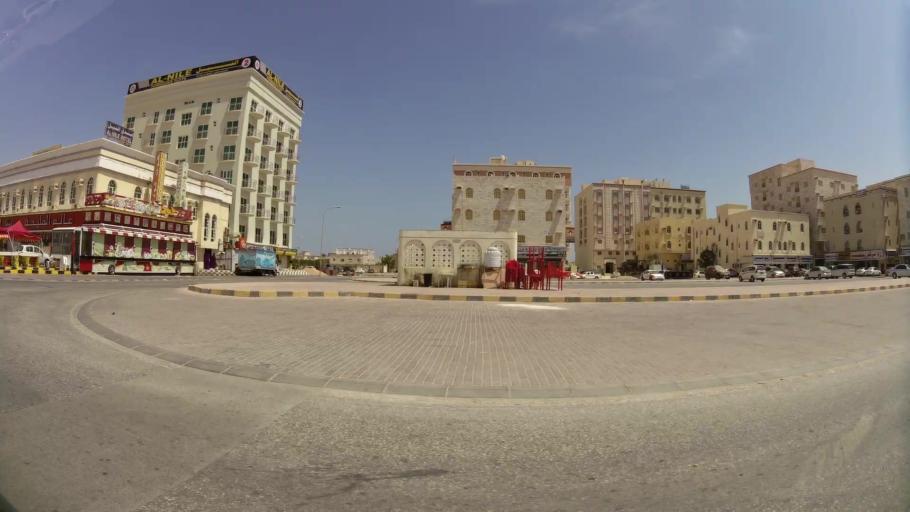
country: OM
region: Zufar
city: Salalah
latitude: 17.0521
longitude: 54.1519
